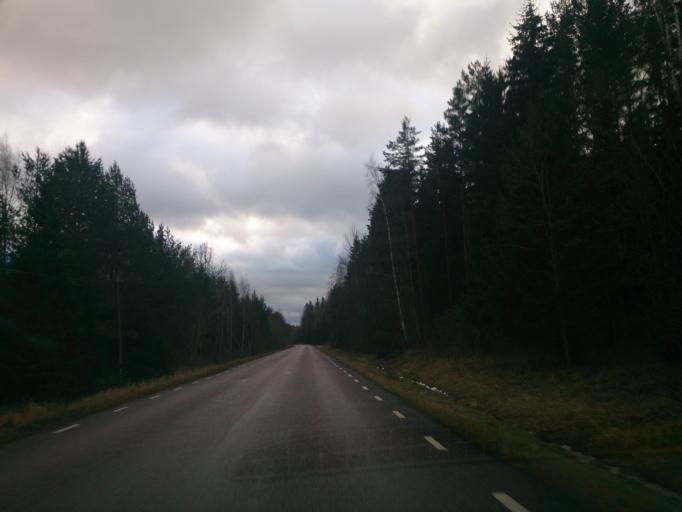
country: SE
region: OEstergoetland
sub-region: Atvidabergs Kommun
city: Atvidaberg
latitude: 58.3240
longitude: 16.0263
